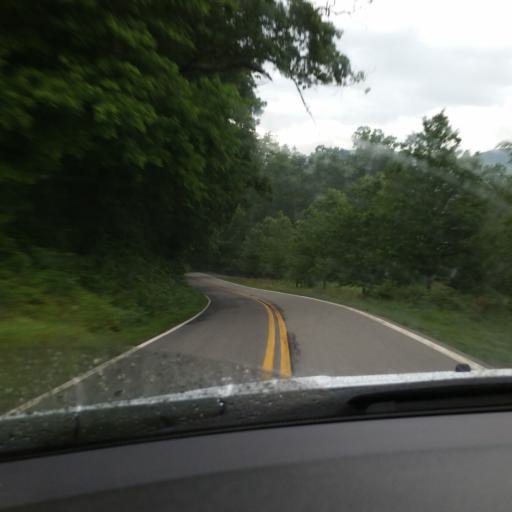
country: US
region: North Carolina
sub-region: Yancey County
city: Burnsville
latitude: 35.8306
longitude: -82.1916
